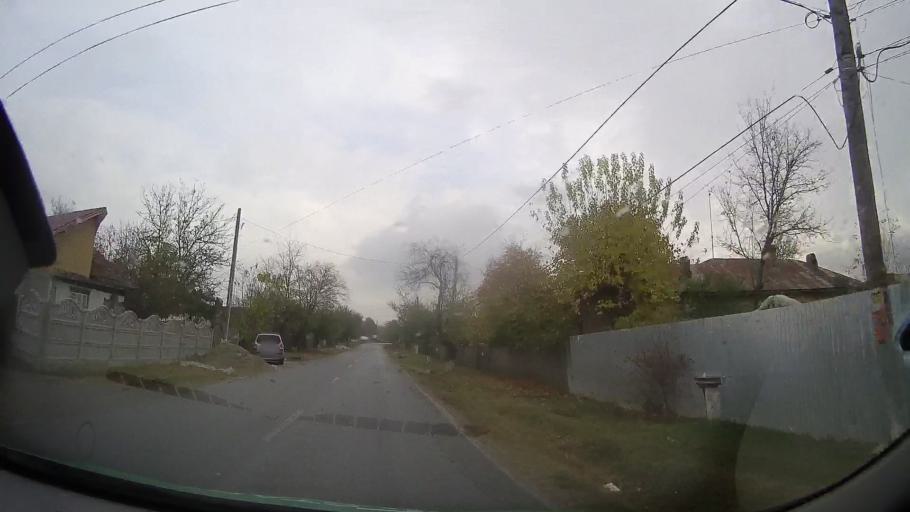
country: RO
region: Prahova
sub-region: Comuna Draganesti
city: Draganesti
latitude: 44.7927
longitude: 26.3085
